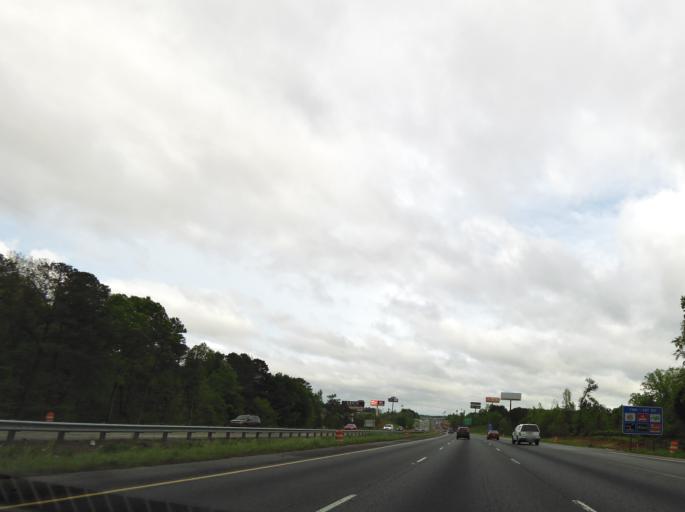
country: US
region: Georgia
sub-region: Henry County
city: Stockbridge
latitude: 33.4764
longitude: -84.2158
